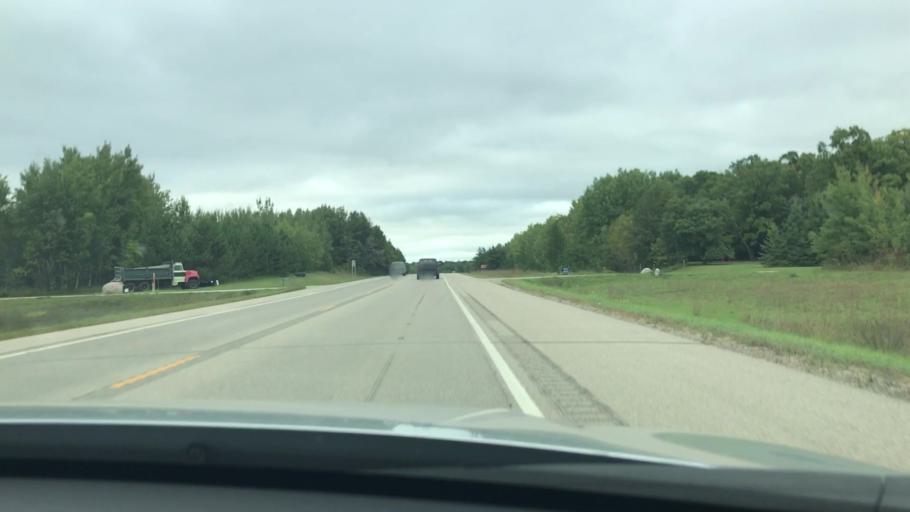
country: US
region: Minnesota
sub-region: Wadena County
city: Menahga
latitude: 46.8362
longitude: -95.0867
